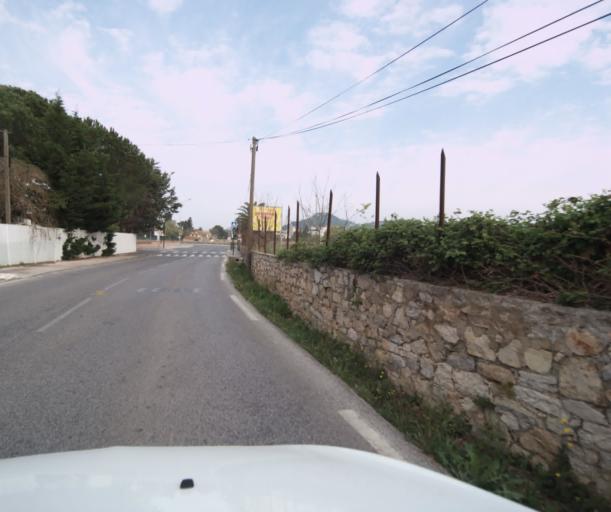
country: FR
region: Provence-Alpes-Cote d'Azur
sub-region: Departement du Var
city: Hyeres
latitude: 43.1095
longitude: 6.1401
